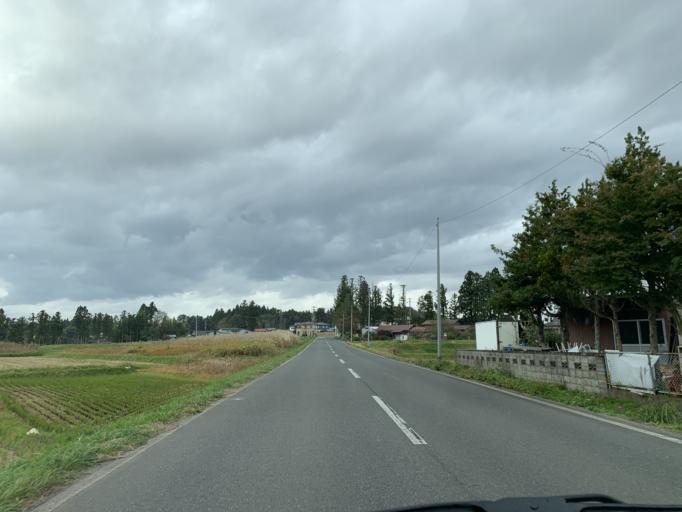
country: JP
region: Iwate
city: Mizusawa
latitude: 39.0562
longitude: 141.1110
